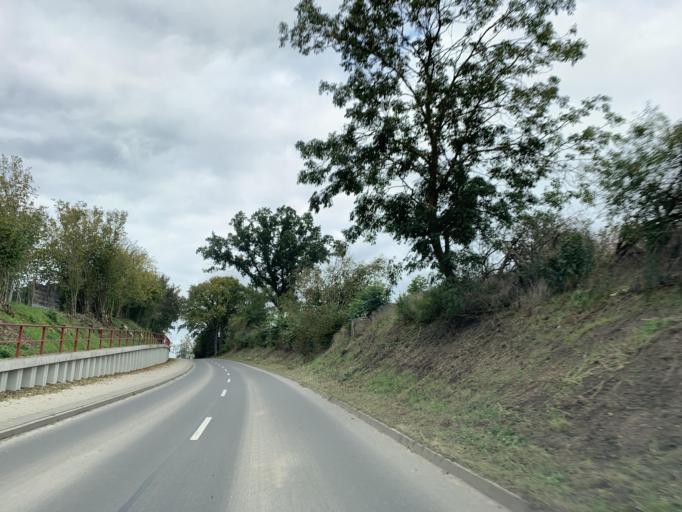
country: DE
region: Mecklenburg-Vorpommern
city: Blankensee
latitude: 53.4153
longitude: 13.2639
